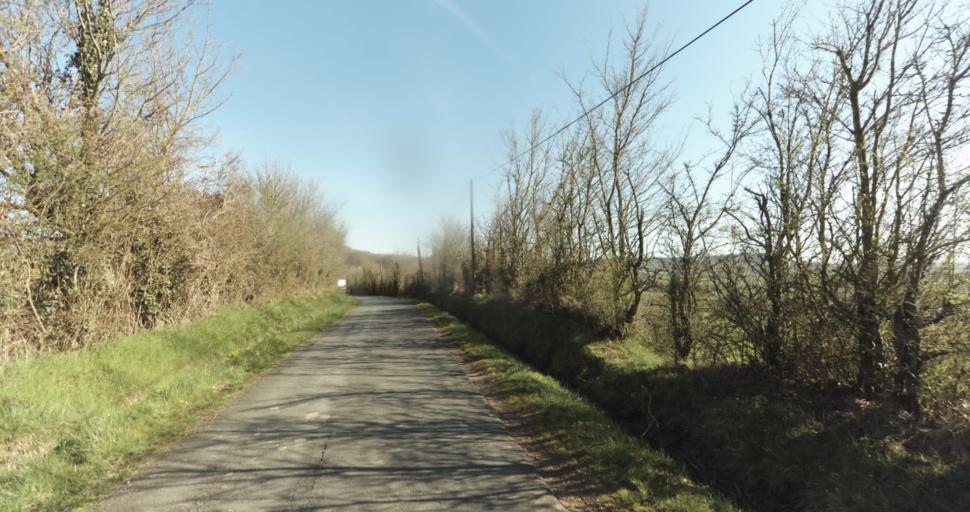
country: FR
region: Lower Normandy
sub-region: Departement du Calvados
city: Saint-Pierre-sur-Dives
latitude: 49.0443
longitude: 0.0367
